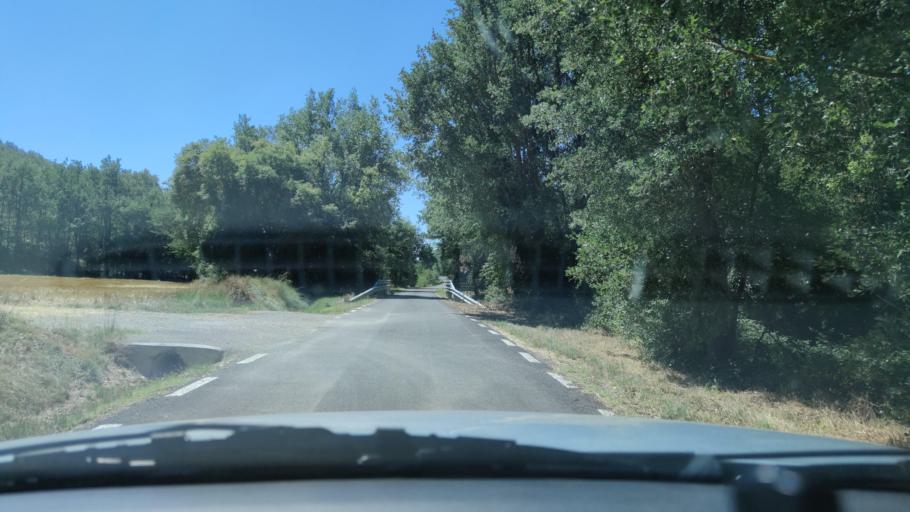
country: ES
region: Catalonia
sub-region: Provincia de Lleida
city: Tora de Riubregos
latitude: 41.8916
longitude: 1.4405
